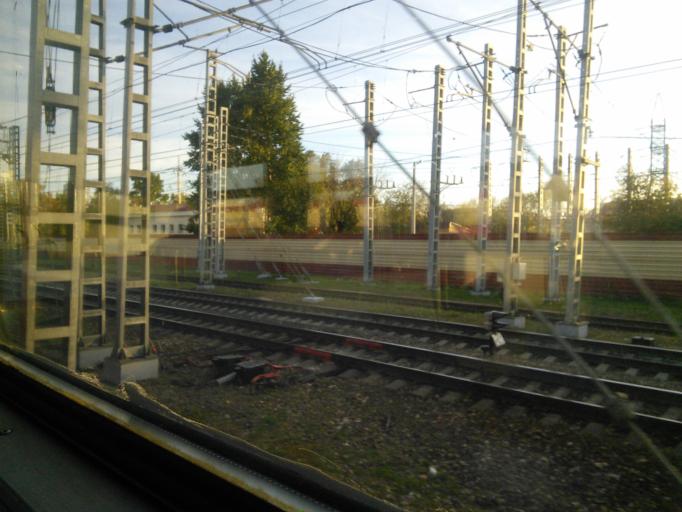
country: RU
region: Moscow
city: Ostankinskiy
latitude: 55.8154
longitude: 37.6065
